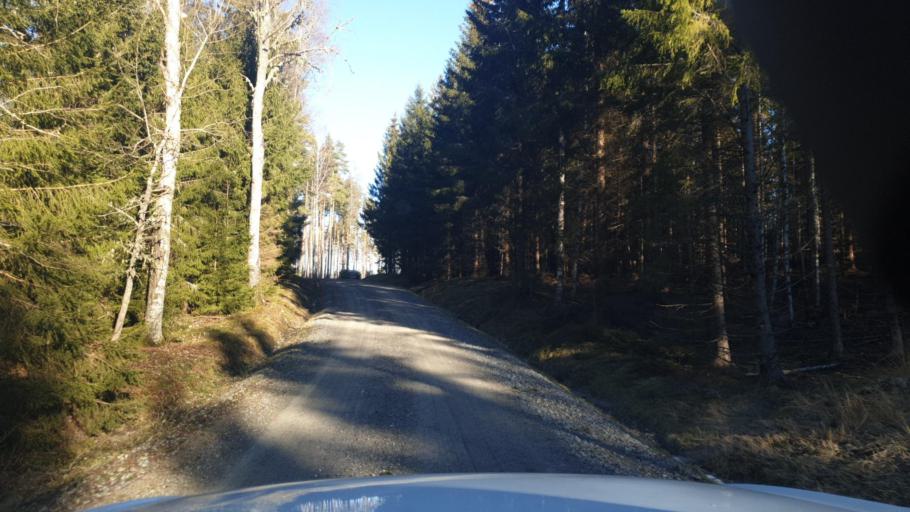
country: SE
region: Vaermland
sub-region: Karlstads Kommun
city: Edsvalla
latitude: 59.4629
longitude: 13.1200
